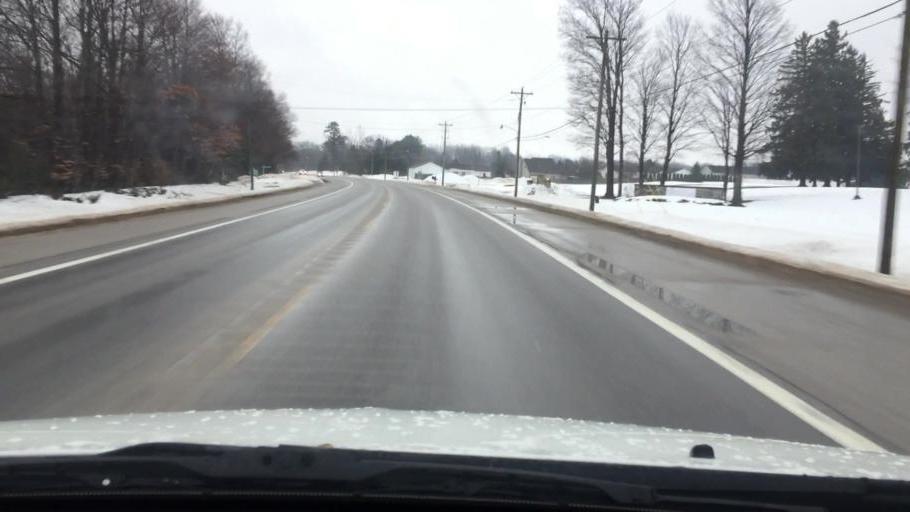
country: US
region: Michigan
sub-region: Charlevoix County
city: Charlevoix
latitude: 45.2832
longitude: -85.2394
